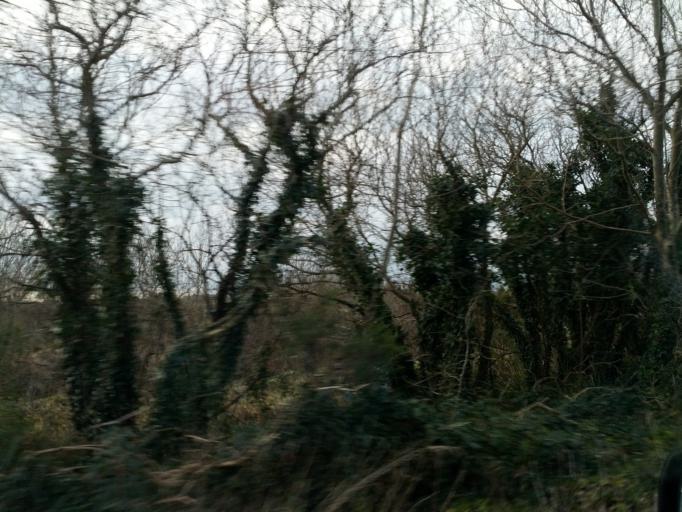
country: IE
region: Connaught
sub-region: County Galway
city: Athenry
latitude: 53.3560
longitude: -8.6695
